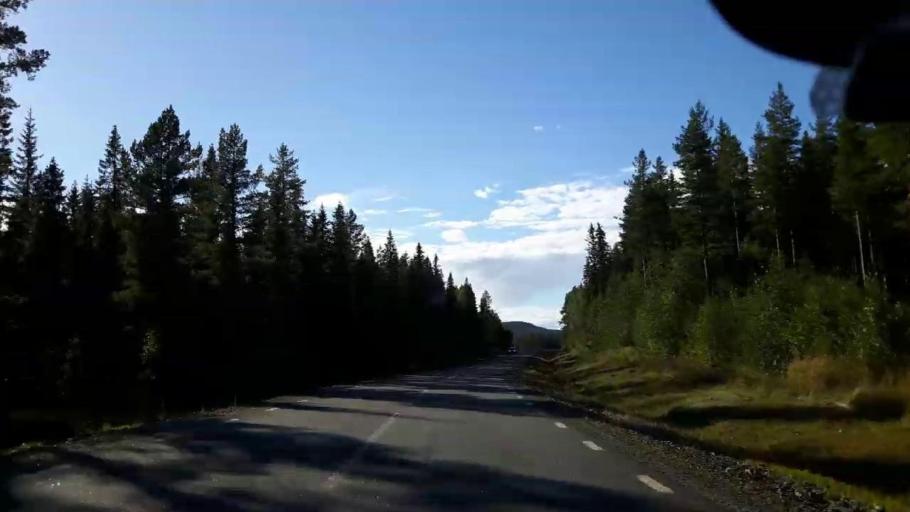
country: SE
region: Jaemtland
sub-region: Stroemsunds Kommun
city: Stroemsund
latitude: 63.5381
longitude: 15.9979
